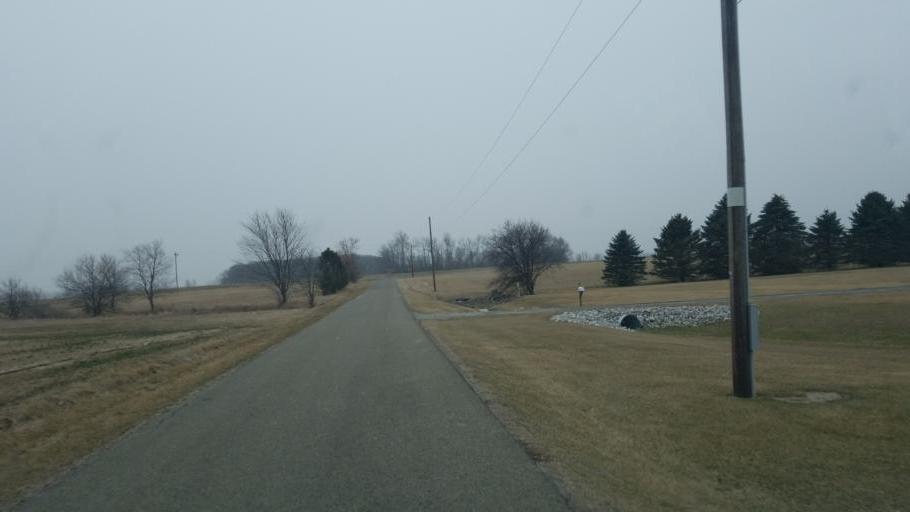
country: US
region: Ohio
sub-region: Defiance County
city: Hicksville
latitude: 41.3267
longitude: -84.7383
